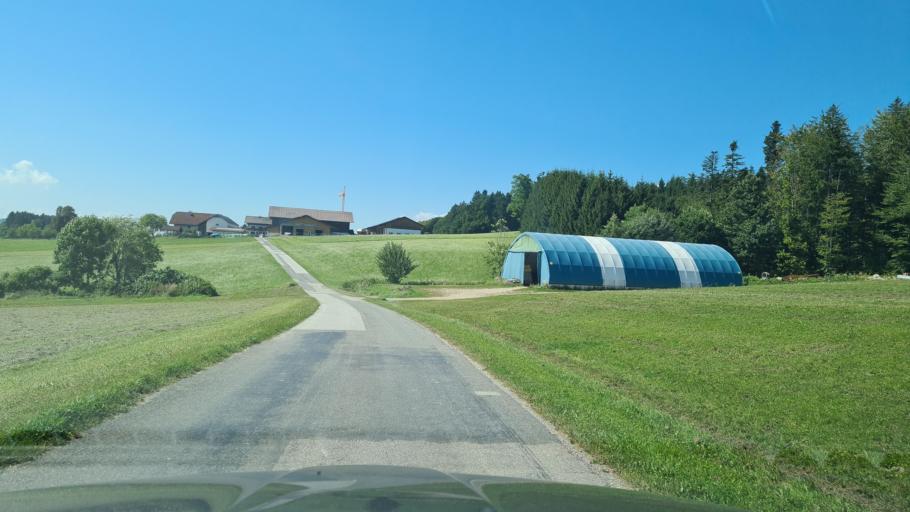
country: AT
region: Salzburg
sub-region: Politischer Bezirk Salzburg-Umgebung
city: Schleedorf
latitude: 47.9719
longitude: 13.1622
